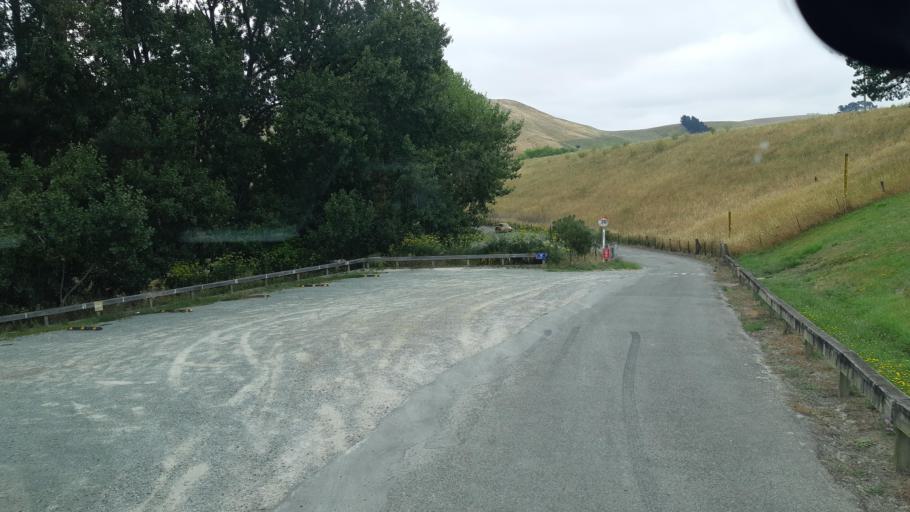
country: NZ
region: Marlborough
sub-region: Marlborough District
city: Blenheim
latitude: -41.5719
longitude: 173.9328
